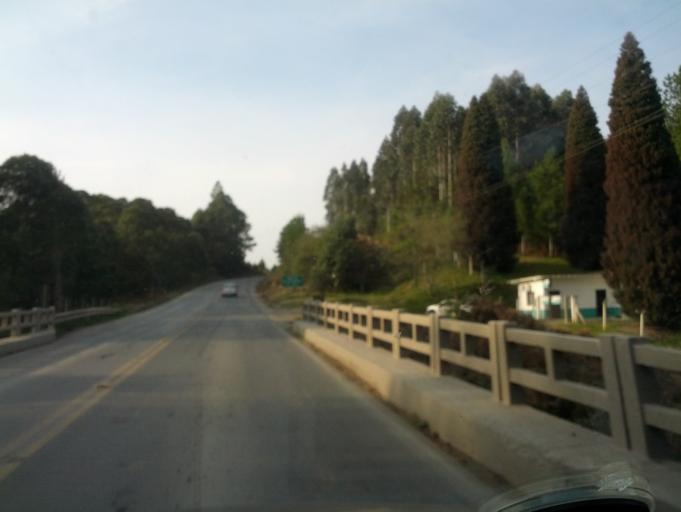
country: BR
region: Santa Catarina
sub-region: Otacilio Costa
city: Otacilio Costa
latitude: -27.5859
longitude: -50.1658
